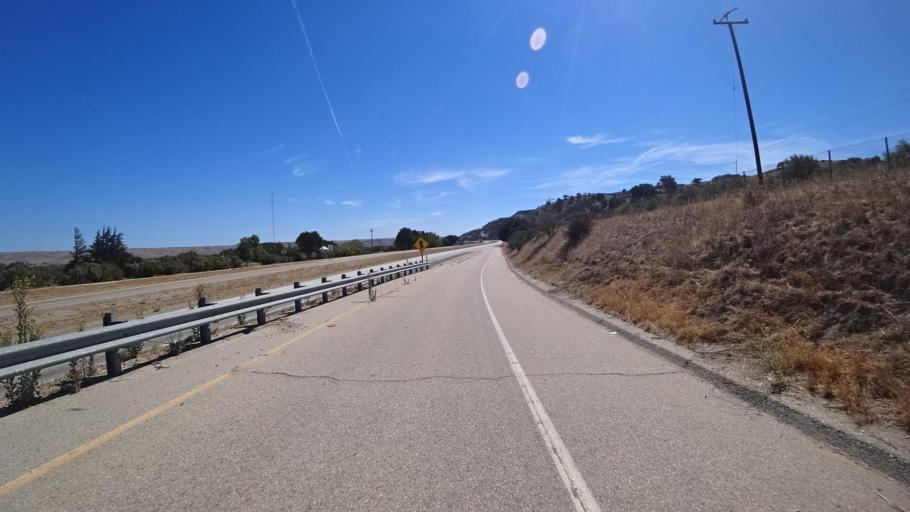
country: US
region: California
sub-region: San Luis Obispo County
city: Lake Nacimiento
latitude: 35.9748
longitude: -120.8997
